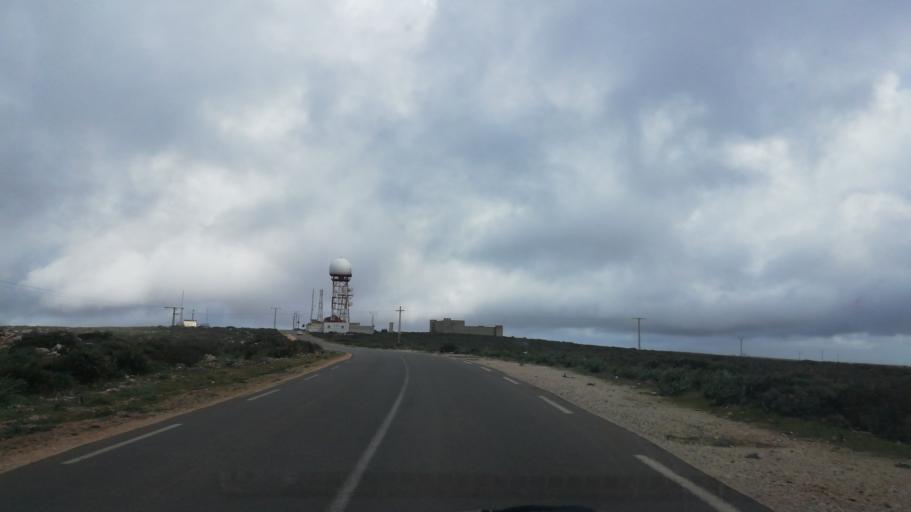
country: DZ
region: Oran
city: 'Ain el Turk
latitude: 35.6940
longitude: -0.7738
